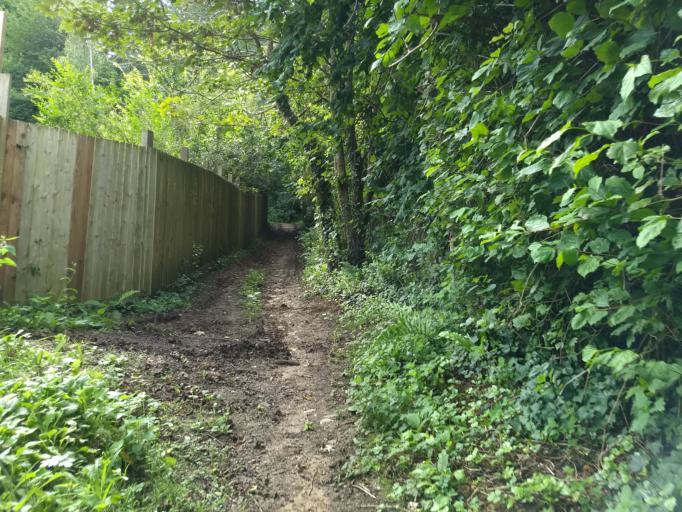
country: GB
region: England
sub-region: Isle of Wight
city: Newport
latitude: 50.6802
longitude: -1.2967
